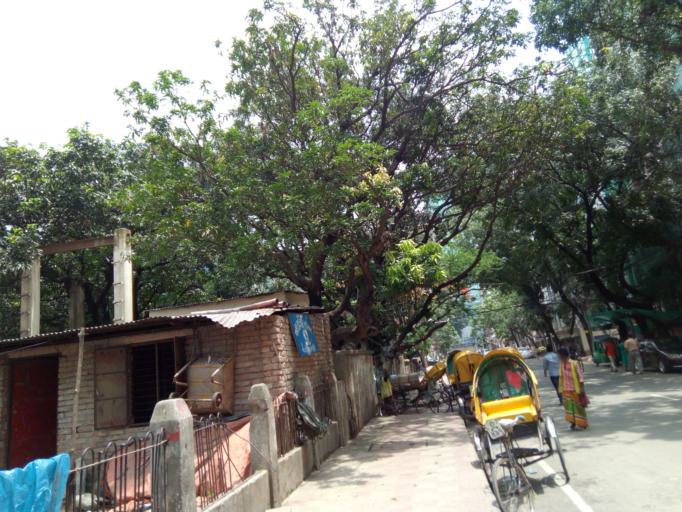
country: BD
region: Dhaka
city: Paltan
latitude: 23.7916
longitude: 90.4040
